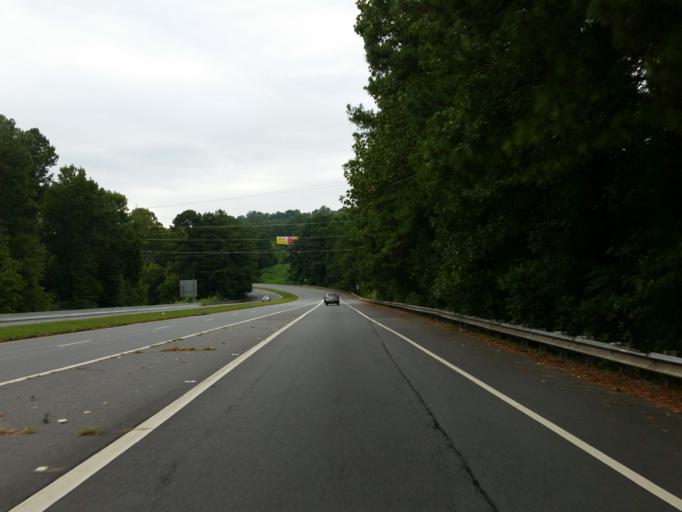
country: US
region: Georgia
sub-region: Cobb County
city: Marietta
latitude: 33.9631
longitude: -84.4986
